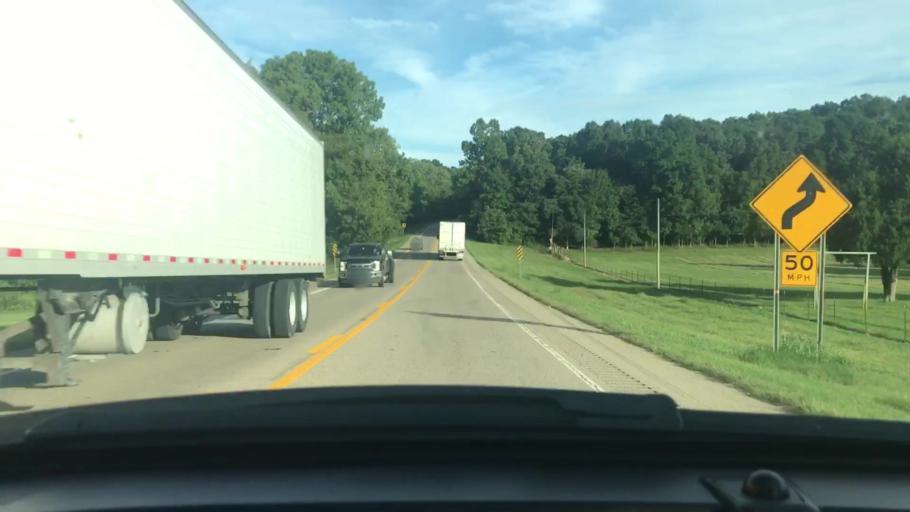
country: US
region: Arkansas
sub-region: Randolph County
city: Pocahontas
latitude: 36.2179
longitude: -91.2188
